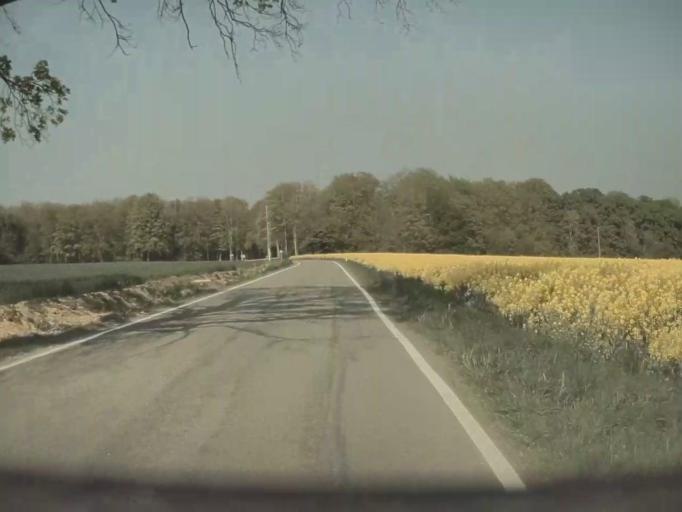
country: BE
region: Wallonia
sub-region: Province de Namur
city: Hamois
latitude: 50.3064
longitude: 5.2257
